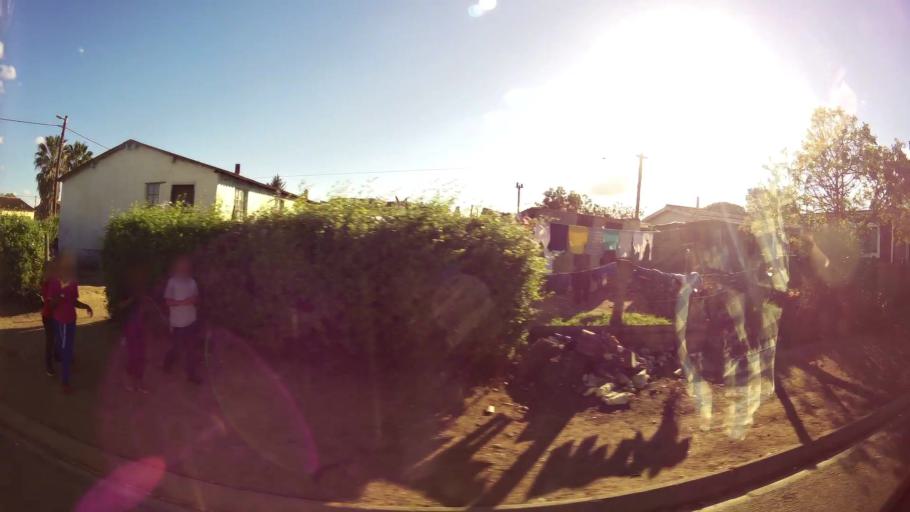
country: ZA
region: Western Cape
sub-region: Eden District Municipality
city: Riversdale
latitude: -34.1055
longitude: 20.9634
